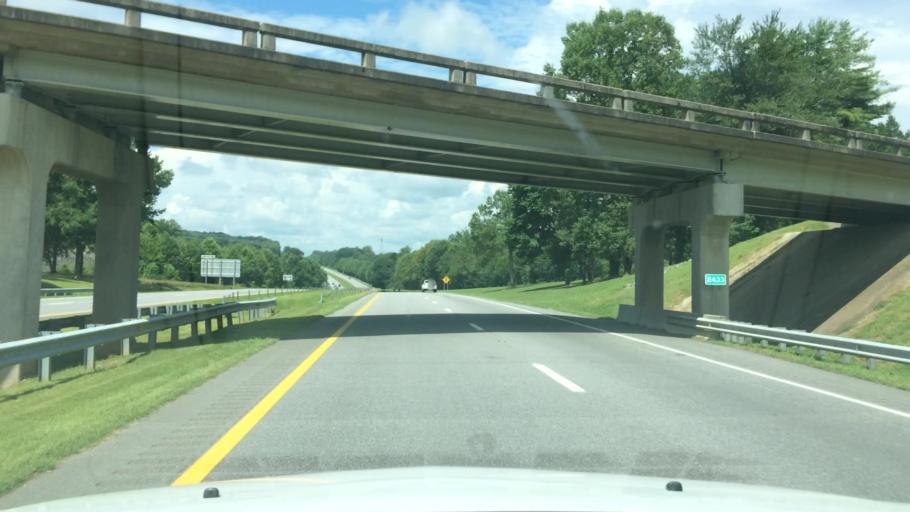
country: US
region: North Carolina
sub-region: Wilkes County
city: North Wilkesboro
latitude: 36.1505
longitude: -81.0179
